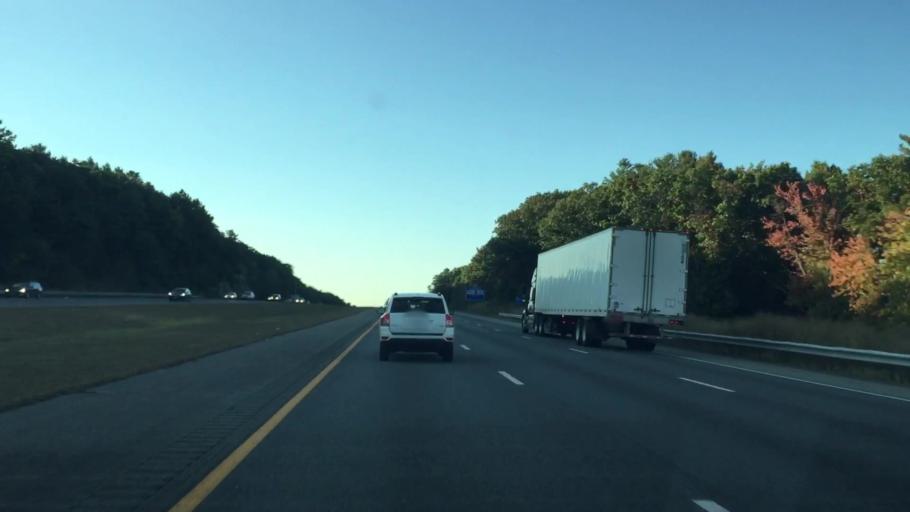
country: US
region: Massachusetts
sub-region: Middlesex County
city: Burlington
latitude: 42.4891
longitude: -71.2300
